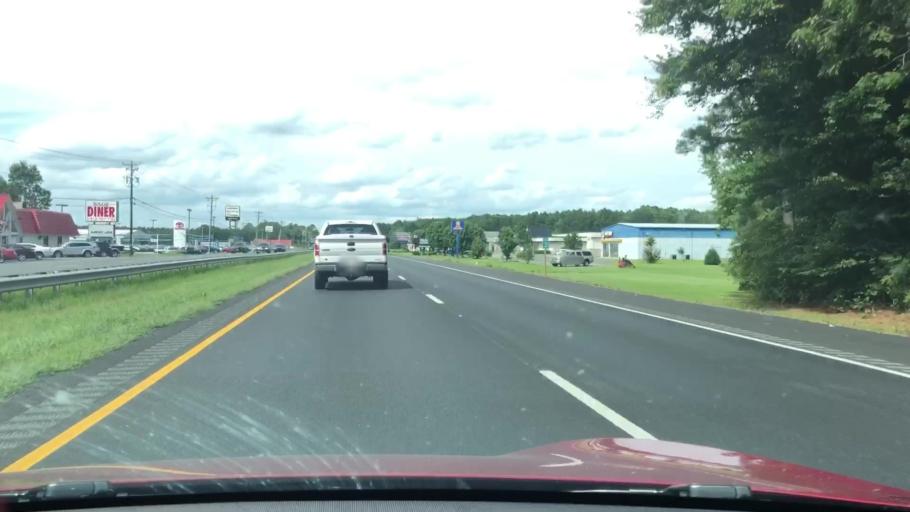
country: US
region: Maryland
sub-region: Worcester County
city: Pocomoke City
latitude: 38.0421
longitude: -75.5424
